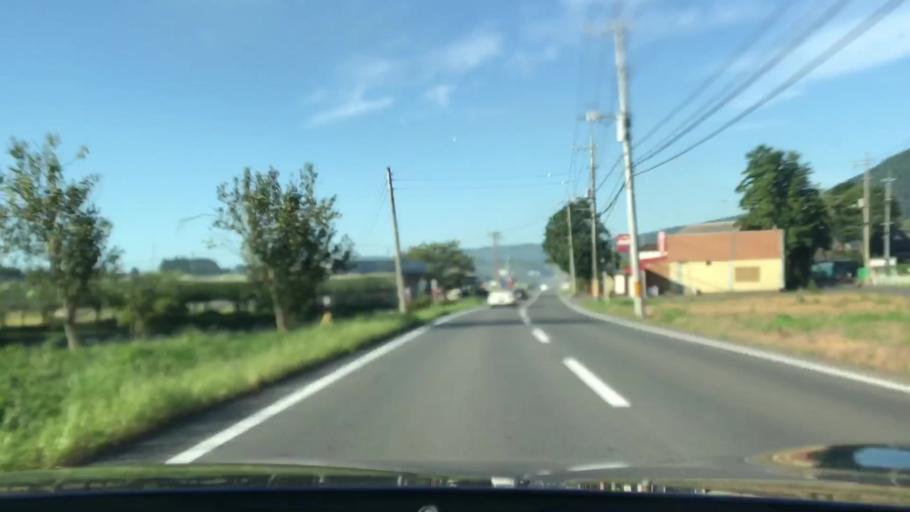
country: JP
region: Ibaraki
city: Makabe
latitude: 36.2595
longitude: 140.1730
